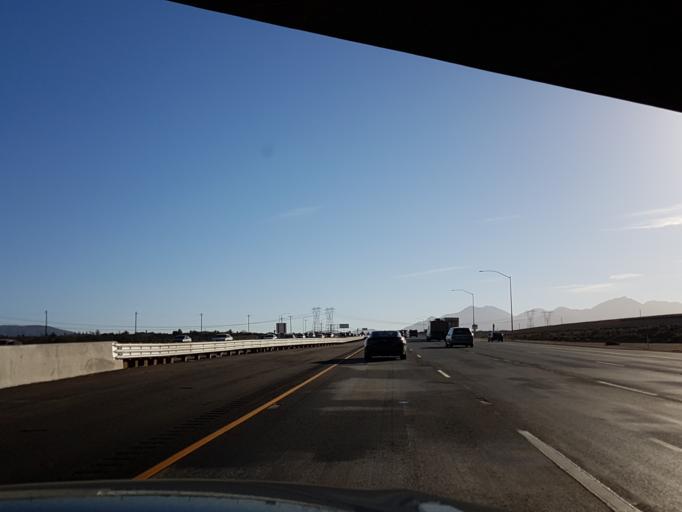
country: US
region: California
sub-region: San Bernardino County
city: Oak Hills
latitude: 34.3830
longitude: -117.4155
